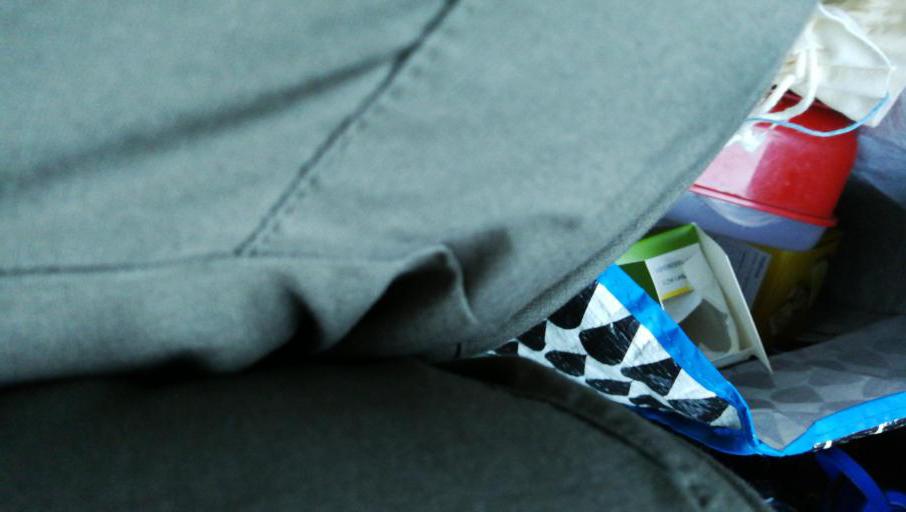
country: GB
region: England
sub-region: Derbyshire
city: Bakewell
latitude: 53.2253
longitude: -1.7043
